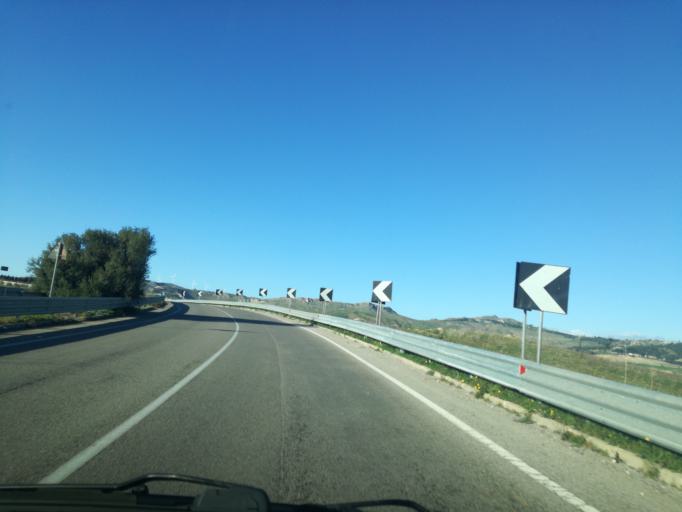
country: IT
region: Sicily
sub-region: Provincia di Caltanissetta
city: Butera
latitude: 37.1310
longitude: 14.1223
